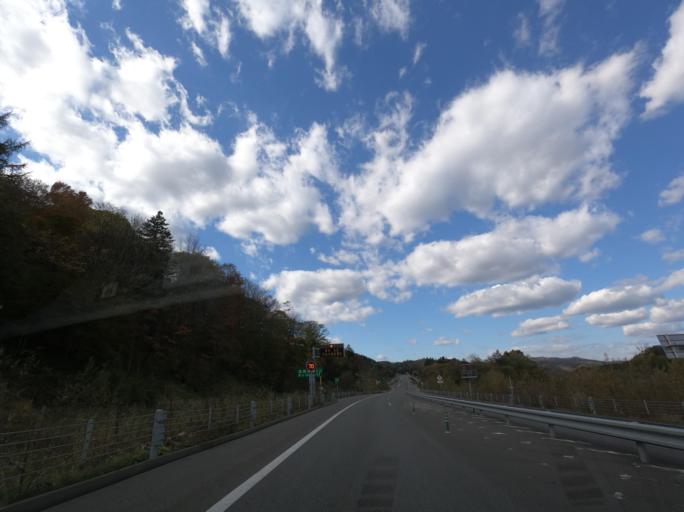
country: JP
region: Hokkaido
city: Kushiro
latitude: 43.0755
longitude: 144.0702
